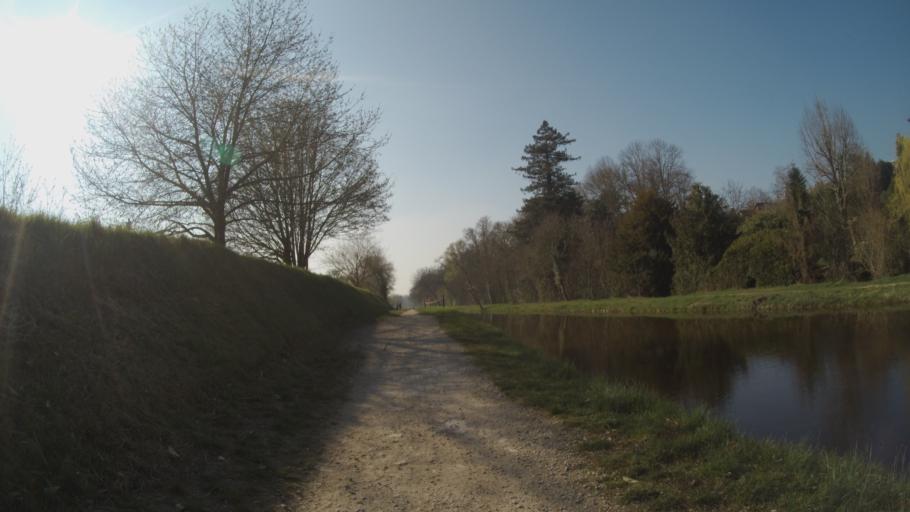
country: FR
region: Centre
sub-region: Departement du Loiret
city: Checy
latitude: 47.8917
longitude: 2.0205
